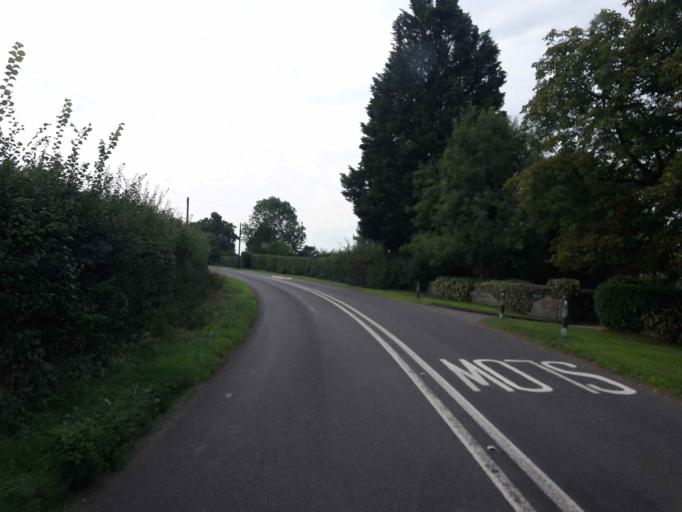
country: GB
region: England
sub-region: West Sussex
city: Billingshurst
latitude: 50.9910
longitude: -0.4069
